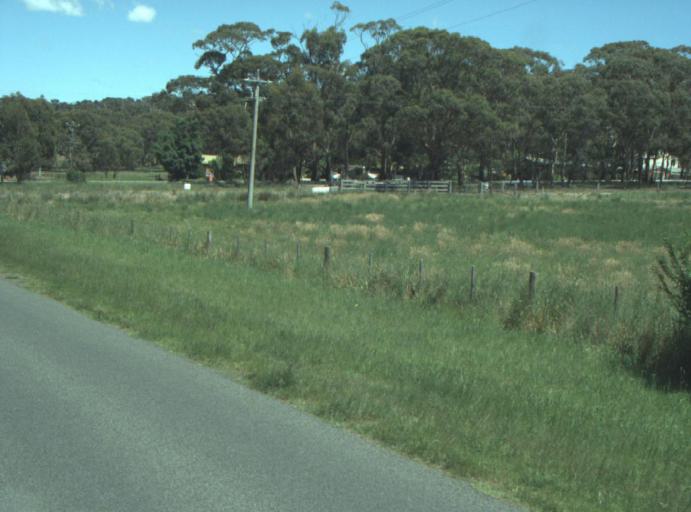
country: AU
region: Victoria
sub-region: Greater Geelong
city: Lara
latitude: -37.8840
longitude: 144.2592
